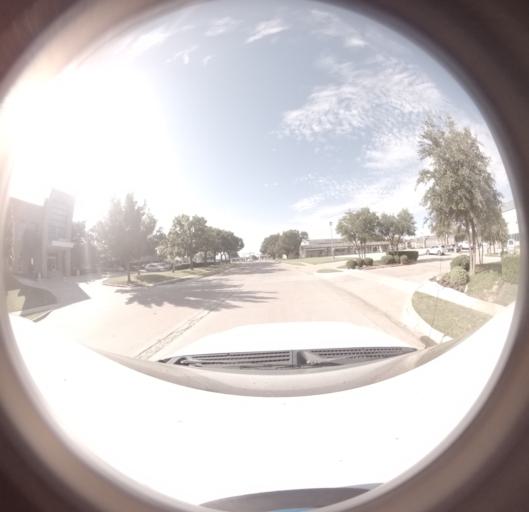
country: US
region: Texas
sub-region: Ector County
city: West Odessa
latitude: 31.7421
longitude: -102.5319
